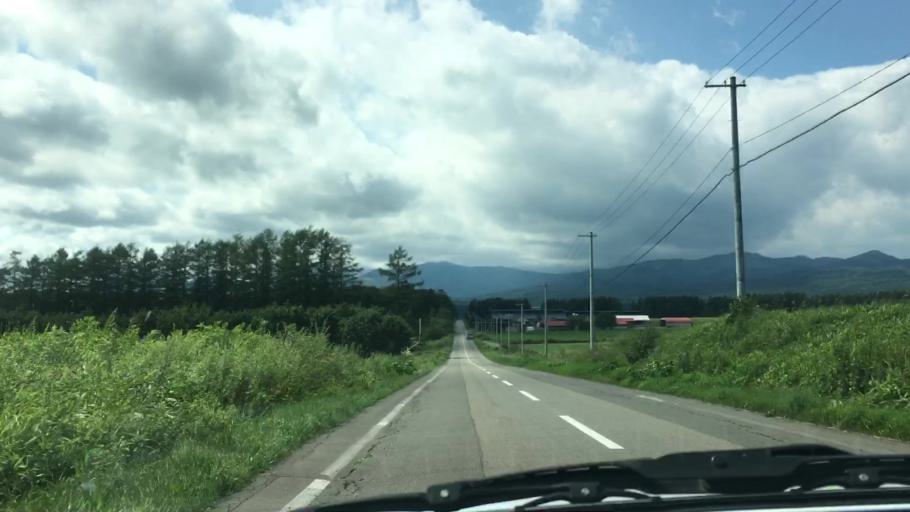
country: JP
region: Hokkaido
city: Otofuke
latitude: 43.2803
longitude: 143.3393
